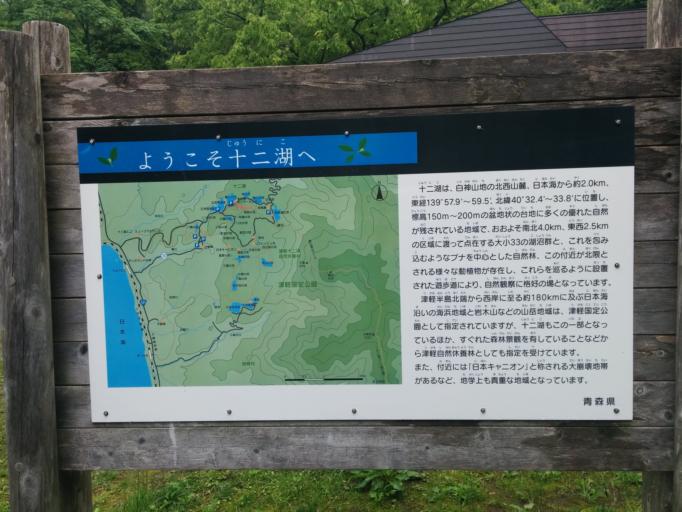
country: JP
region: Akita
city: Noshiromachi
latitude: 40.5655
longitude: 139.9735
